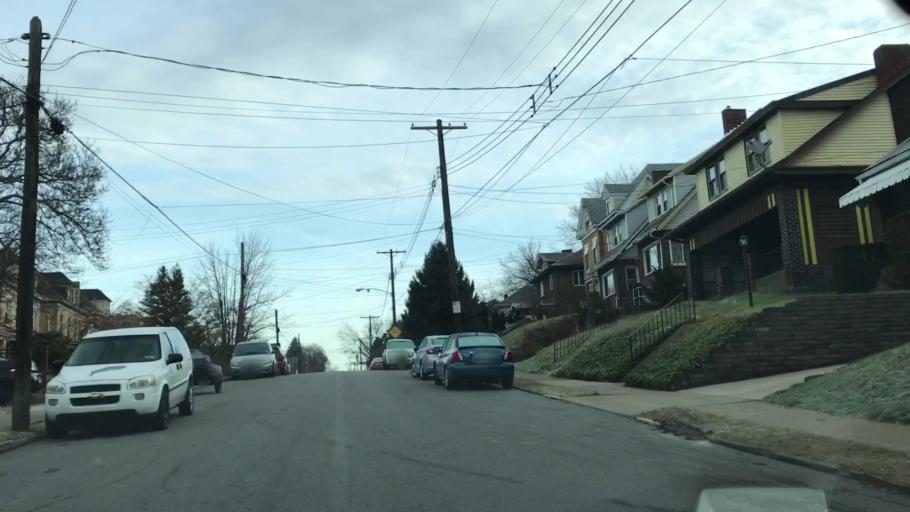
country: US
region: Pennsylvania
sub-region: Allegheny County
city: Bellevue
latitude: 40.4874
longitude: -80.0544
